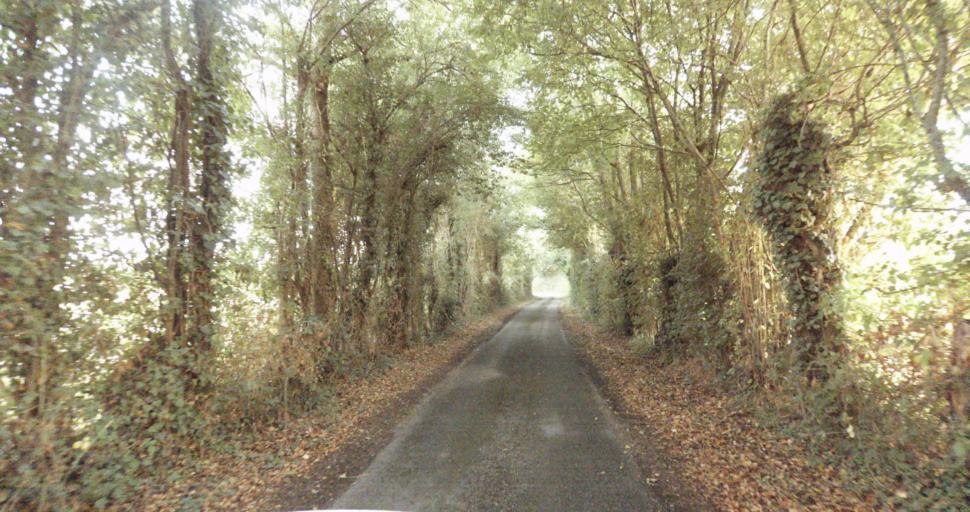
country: FR
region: Lower Normandy
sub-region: Departement de l'Orne
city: Vimoutiers
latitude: 48.9391
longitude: 0.2168
